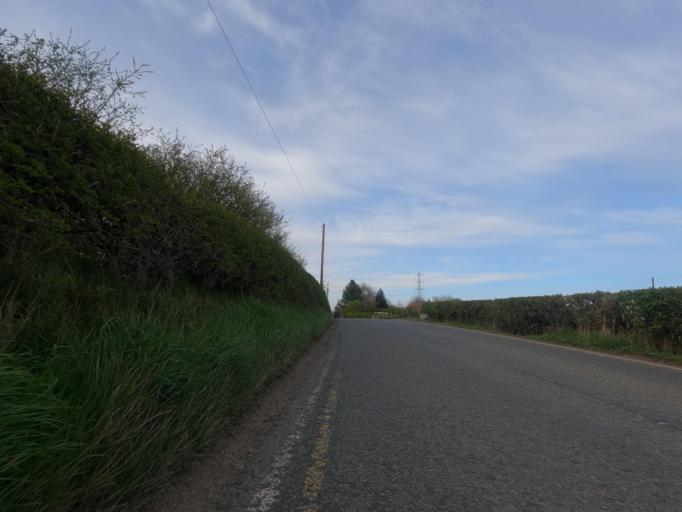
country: GB
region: England
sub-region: Newcastle upon Tyne
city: Hazlerigg
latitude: 55.0237
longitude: -1.6656
